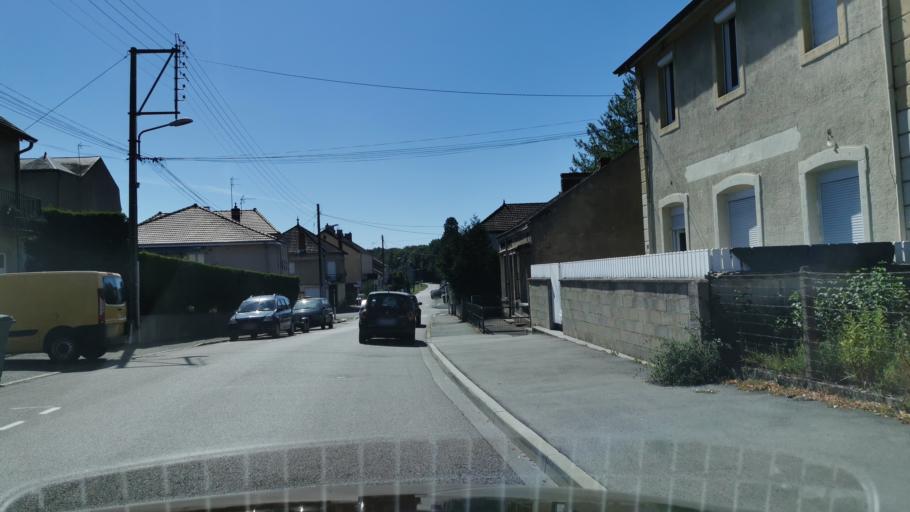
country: FR
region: Bourgogne
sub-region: Departement de Saone-et-Loire
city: Montchanin
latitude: 46.7587
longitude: 4.4796
